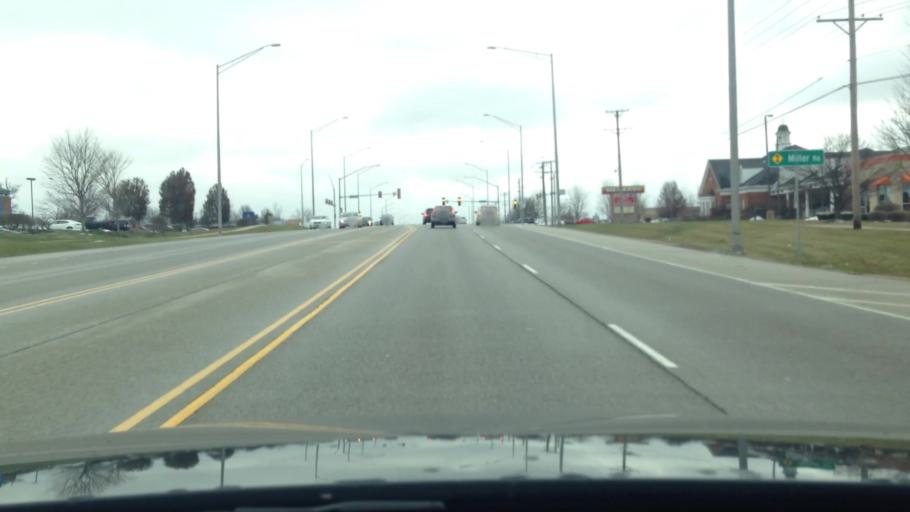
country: US
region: Illinois
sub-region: Kane County
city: Gilberts
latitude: 42.1234
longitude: -88.3355
